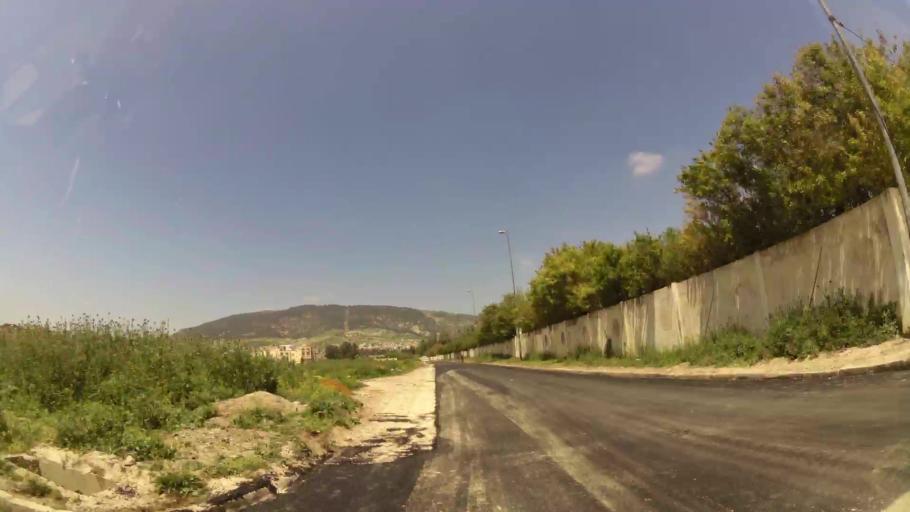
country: MA
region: Fes-Boulemane
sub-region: Fes
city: Fes
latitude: 34.0389
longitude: -5.0457
